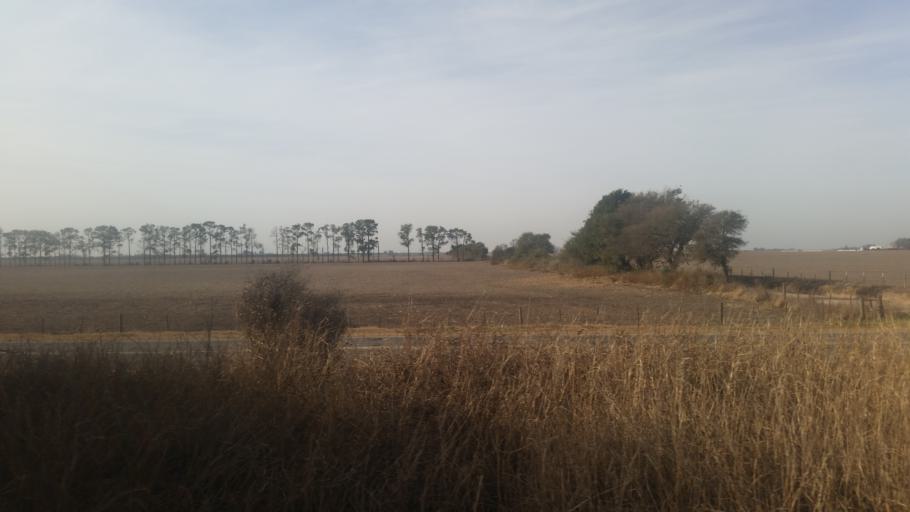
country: AR
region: Cordoba
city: Laguna Larga
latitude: -31.7471
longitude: -63.8293
